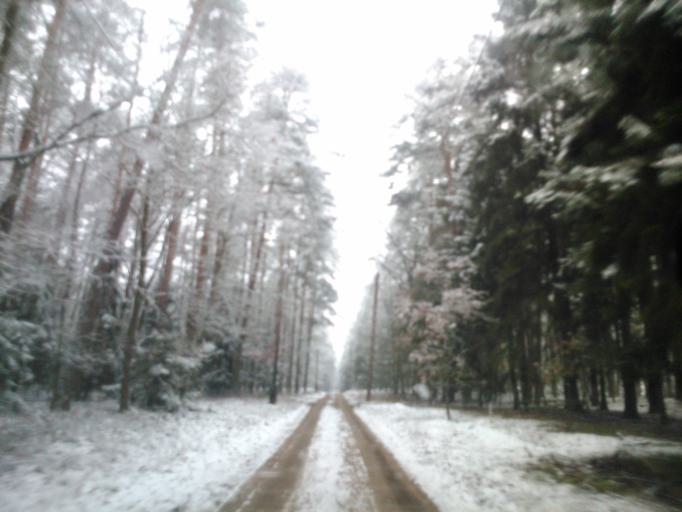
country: PL
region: Kujawsko-Pomorskie
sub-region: Powiat golubsko-dobrzynski
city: Radomin
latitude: 53.1415
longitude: 19.1317
